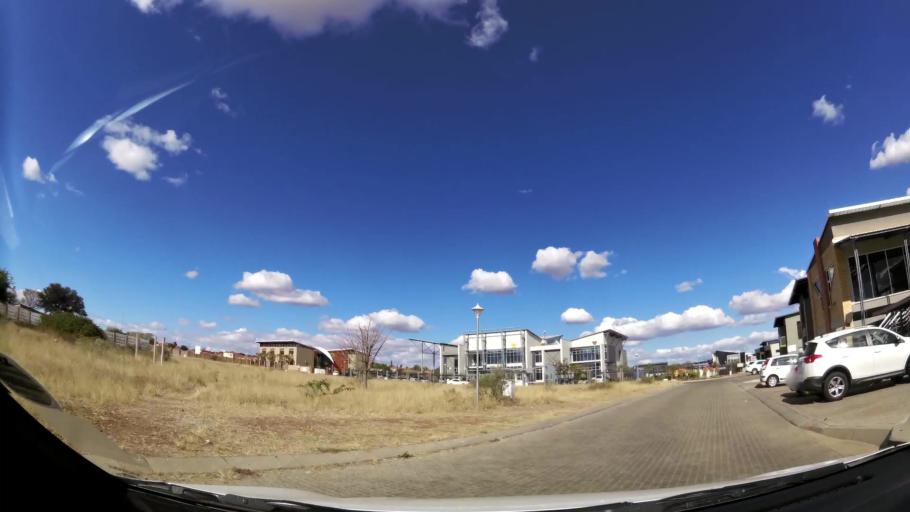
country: ZA
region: Limpopo
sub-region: Capricorn District Municipality
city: Polokwane
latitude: -23.8870
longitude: 29.4735
